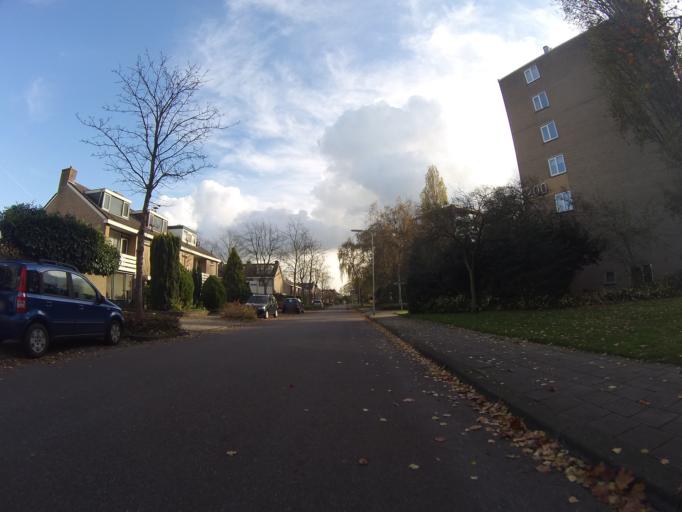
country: NL
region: Gelderland
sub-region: Gemeente Nijkerk
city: Nijkerk
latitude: 52.2166
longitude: 5.4801
